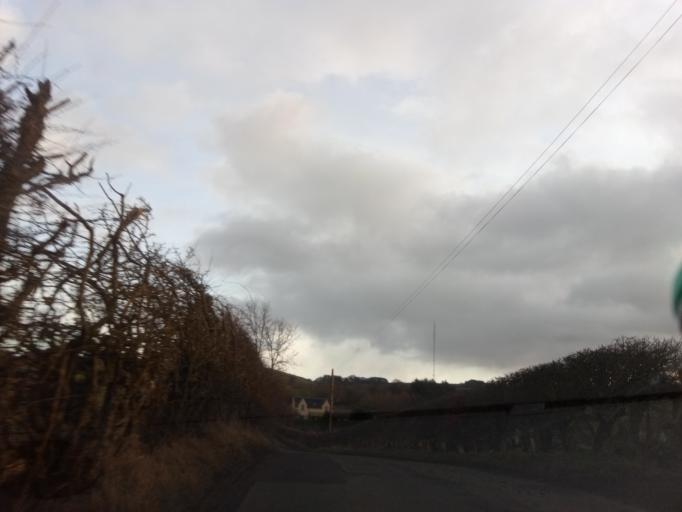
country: GB
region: Scotland
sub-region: The Scottish Borders
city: Selkirk
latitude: 55.5697
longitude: -2.8104
